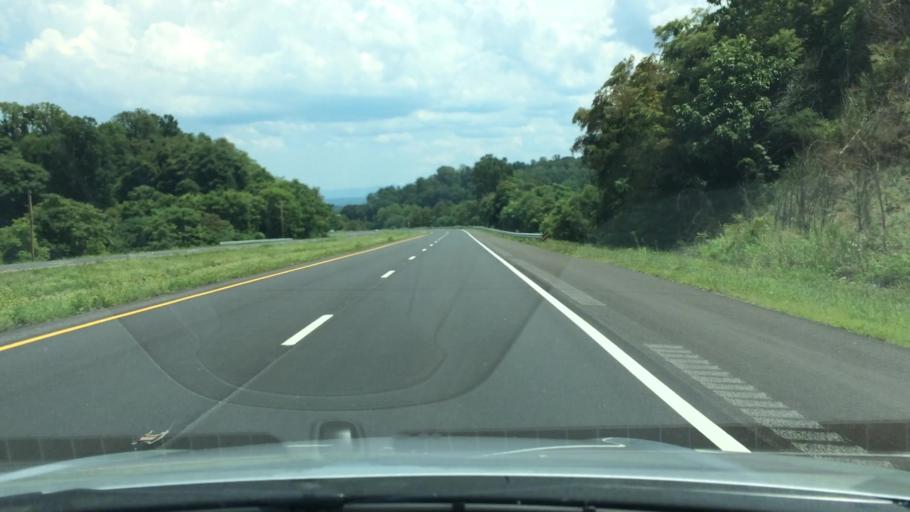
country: US
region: Tennessee
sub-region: Hamblen County
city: Morristown
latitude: 36.1874
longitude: -83.2590
